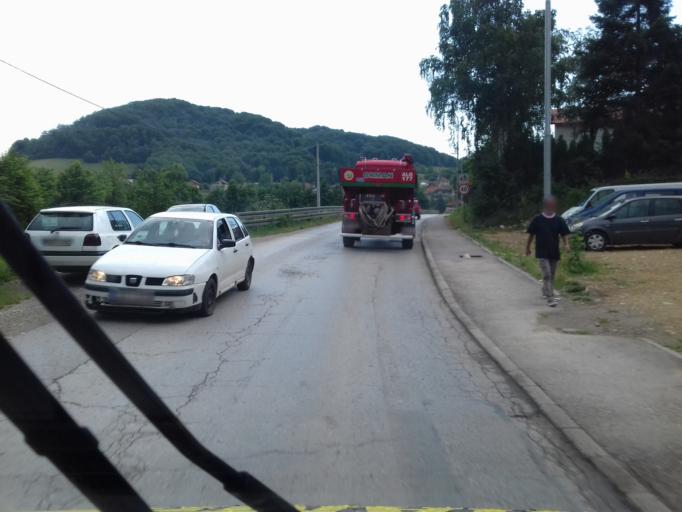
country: BA
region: Federation of Bosnia and Herzegovina
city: Visoko
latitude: 43.9662
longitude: 18.1836
